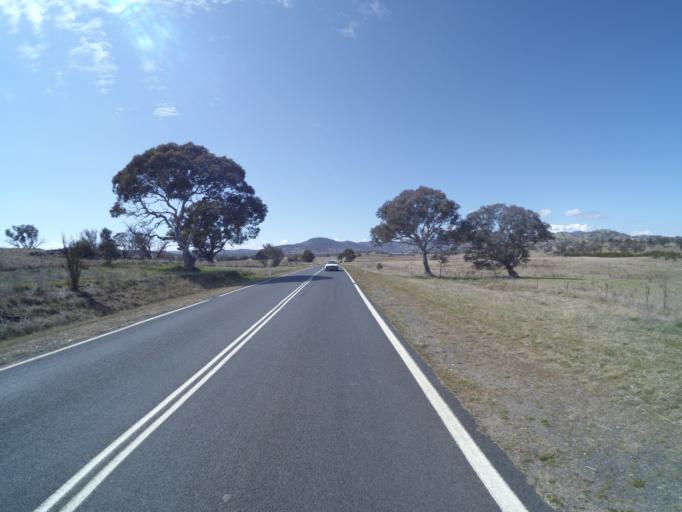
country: AU
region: Australian Capital Territory
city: Macarthur
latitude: -35.4472
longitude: 149.0609
